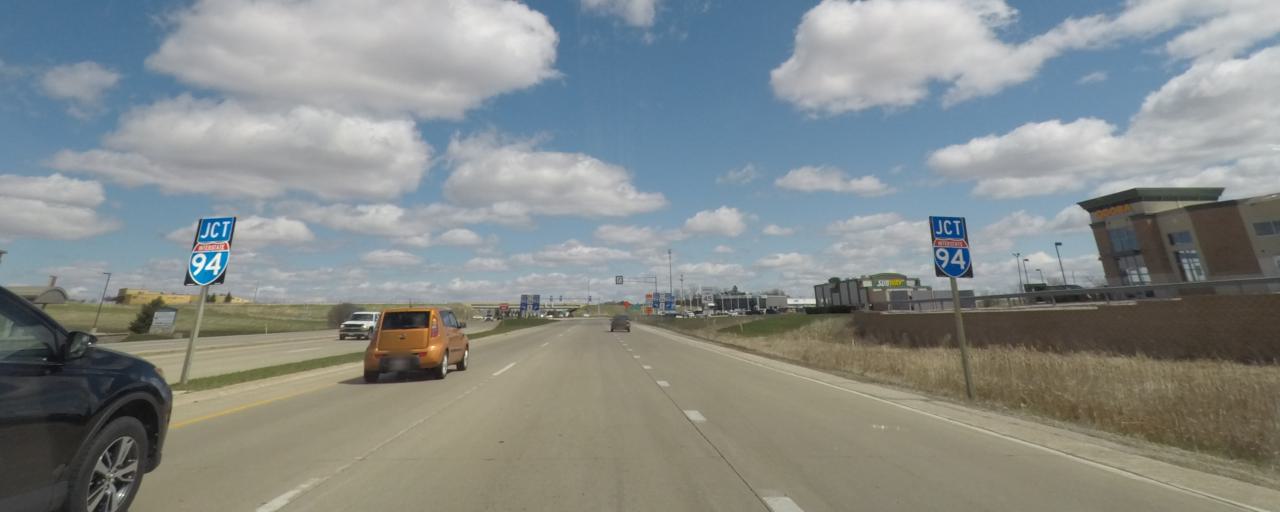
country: US
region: Wisconsin
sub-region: Jefferson County
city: Johnson Creek
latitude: 43.0830
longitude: -88.7630
